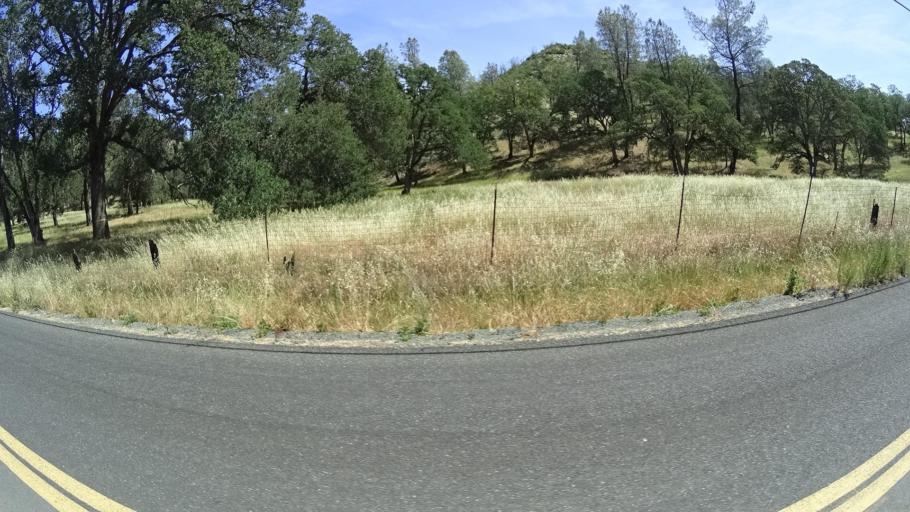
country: US
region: California
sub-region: Lake County
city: Middletown
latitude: 38.7675
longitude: -122.6205
